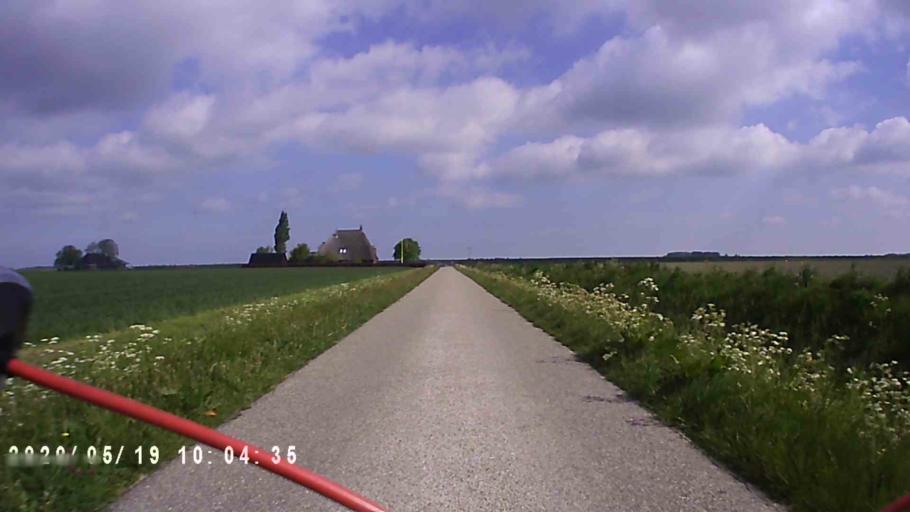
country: NL
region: Friesland
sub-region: Gemeente Kollumerland en Nieuwkruisland
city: Kollum
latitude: 53.3065
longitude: 6.2279
